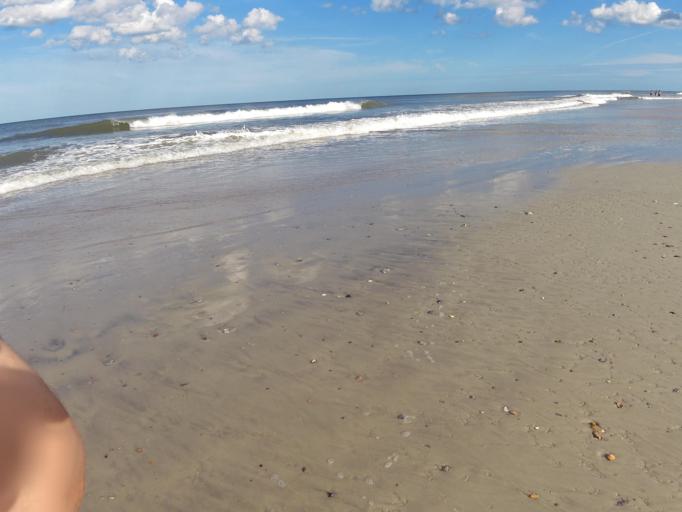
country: US
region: Florida
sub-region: Nassau County
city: Fernandina Beach
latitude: 30.6810
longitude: -81.4282
